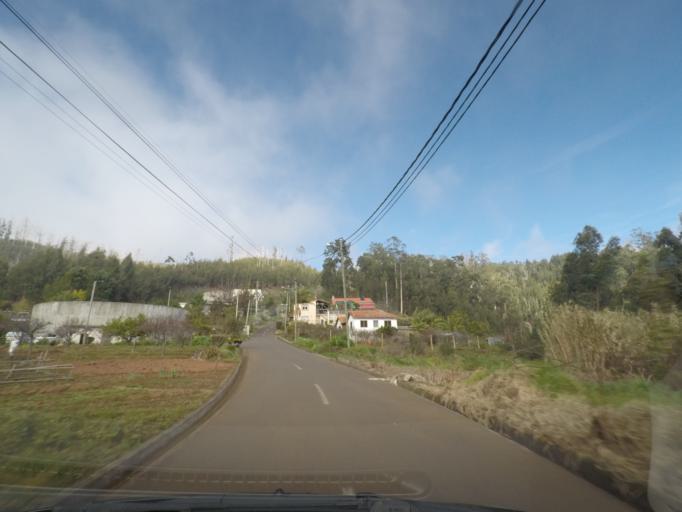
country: PT
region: Madeira
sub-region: Calheta
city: Estreito da Calheta
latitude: 32.7492
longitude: -17.1881
